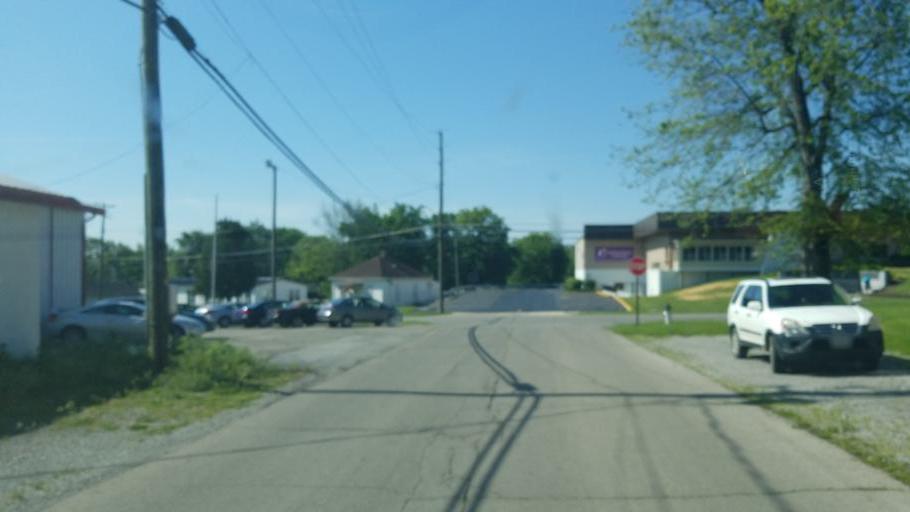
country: US
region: Ohio
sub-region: Hardin County
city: Kenton
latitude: 40.6502
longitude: -83.6198
